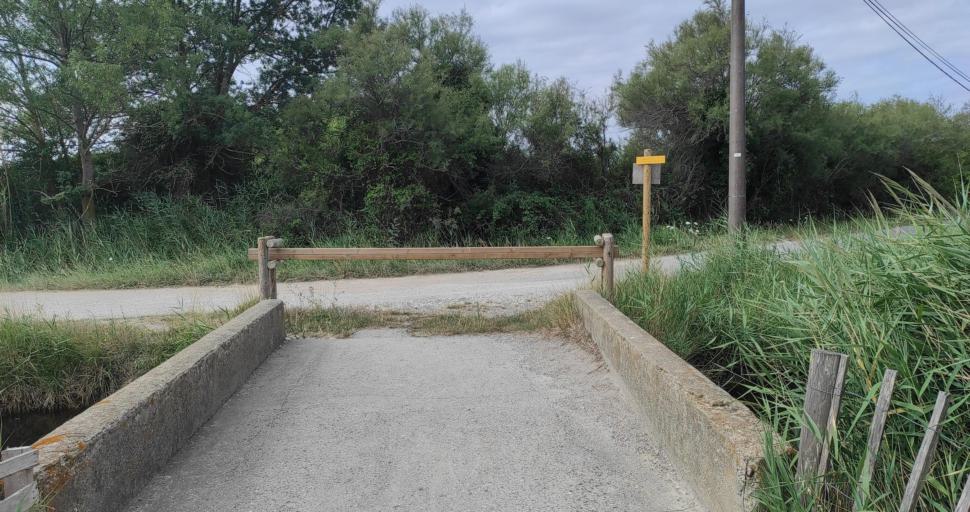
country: FR
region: Languedoc-Roussillon
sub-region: Departement des Pyrenees-Orientales
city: Saint-Hippolyte
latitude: 42.8029
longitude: 2.9730
